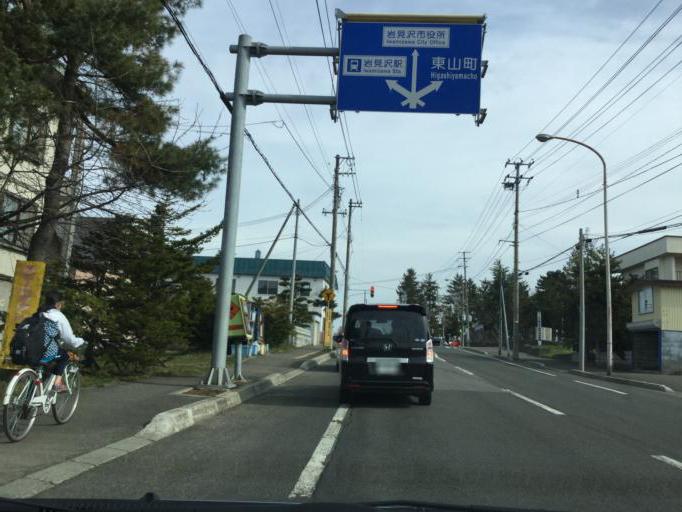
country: JP
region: Hokkaido
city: Iwamizawa
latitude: 43.1872
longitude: 141.7732
